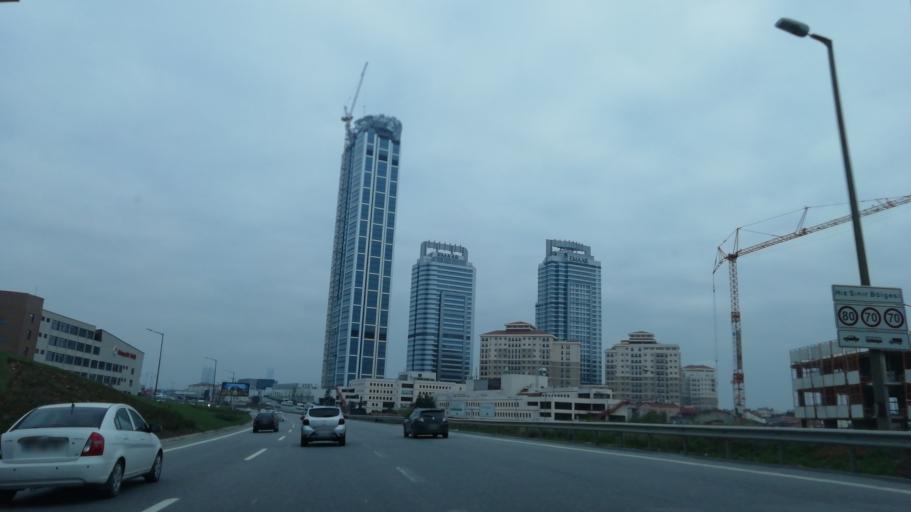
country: TR
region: Istanbul
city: UEskuedar
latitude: 41.0063
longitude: 29.0659
